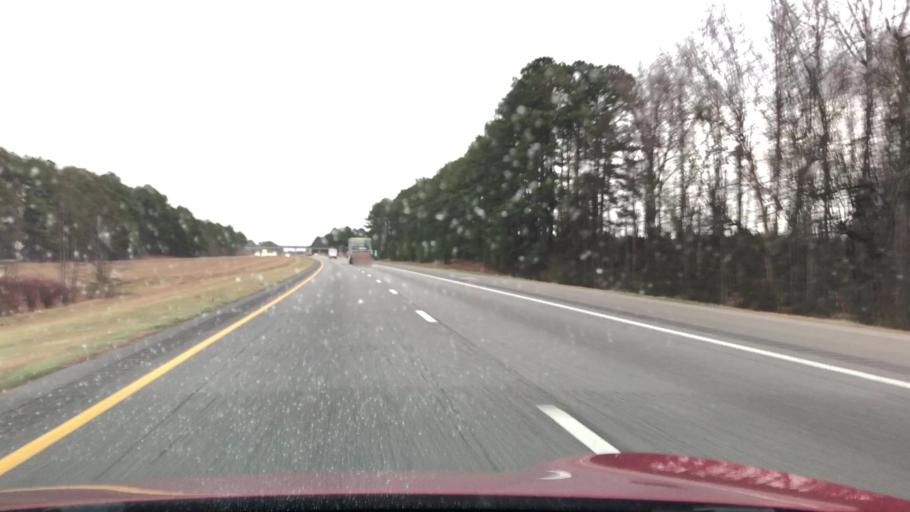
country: US
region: South Carolina
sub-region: Dillon County
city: Latta
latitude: 34.3813
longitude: -79.4736
